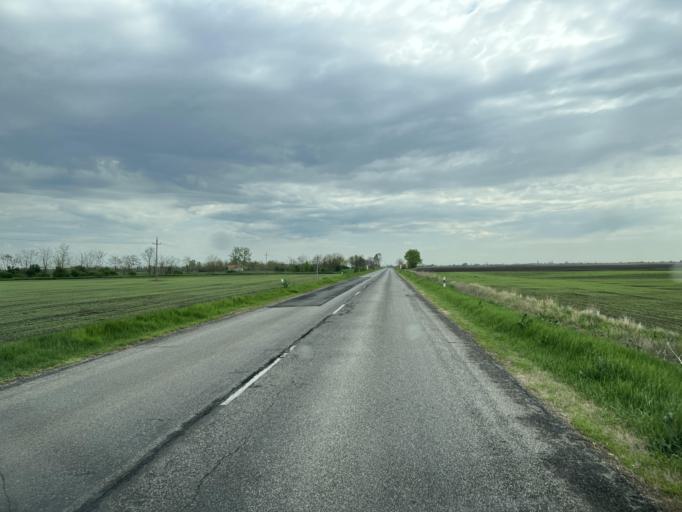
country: HU
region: Pest
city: Abony
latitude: 47.1880
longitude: 19.9518
